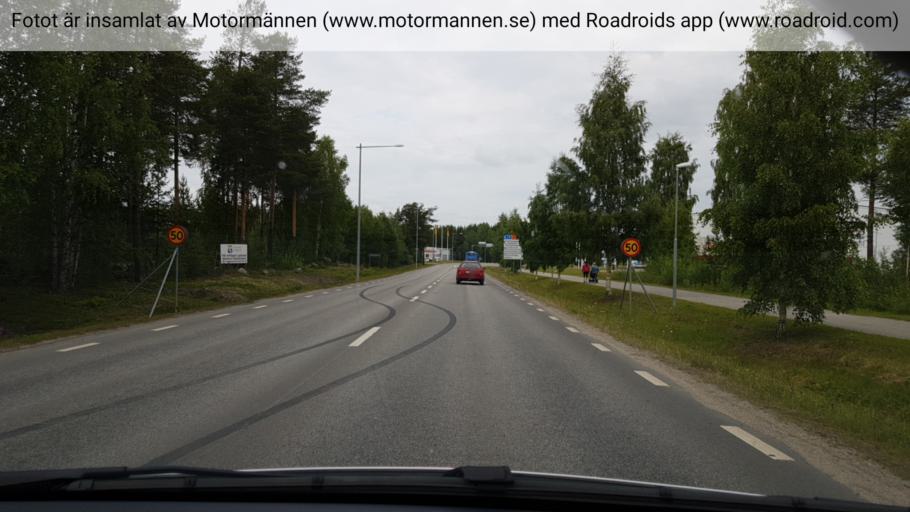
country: SE
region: Vaesterbotten
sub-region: Lycksele Kommun
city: Lycksele
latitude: 64.5836
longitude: 18.6976
